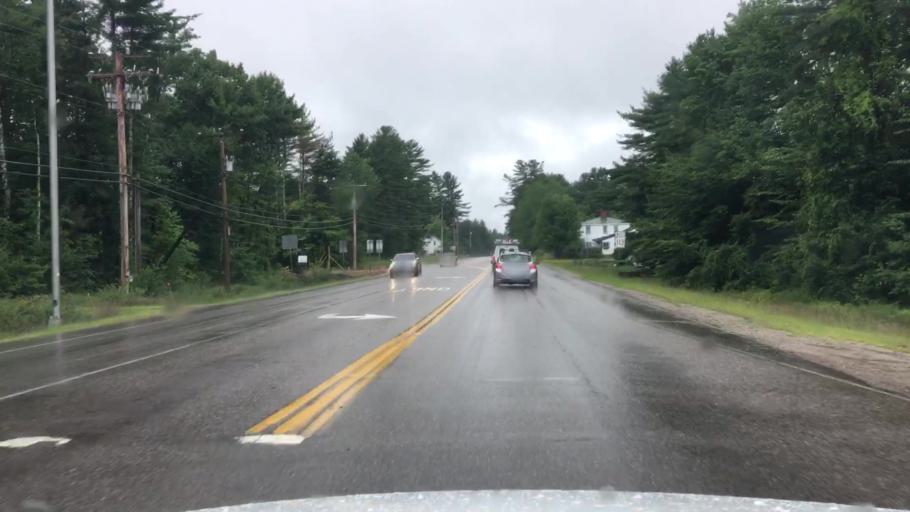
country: US
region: New Hampshire
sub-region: Carroll County
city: Conway
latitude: 43.9928
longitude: -71.0834
